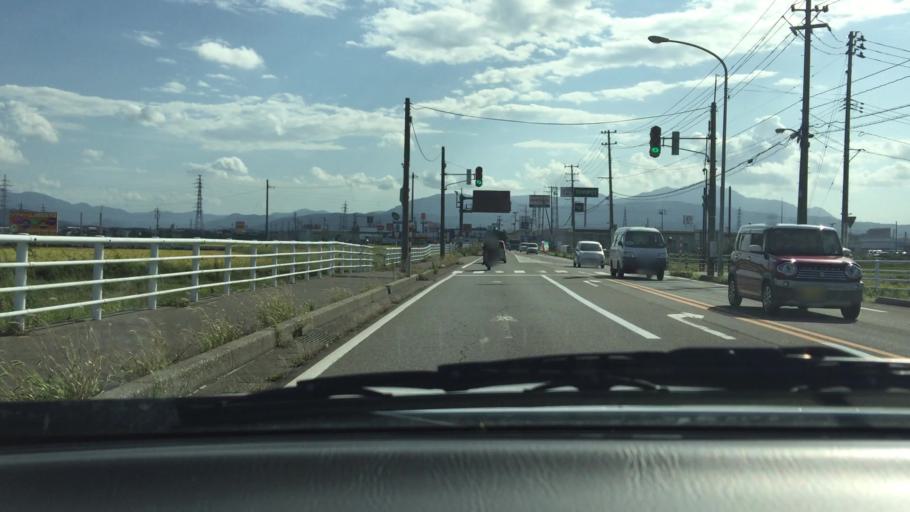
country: JP
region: Niigata
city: Kashiwazaki
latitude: 37.3834
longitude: 138.5831
